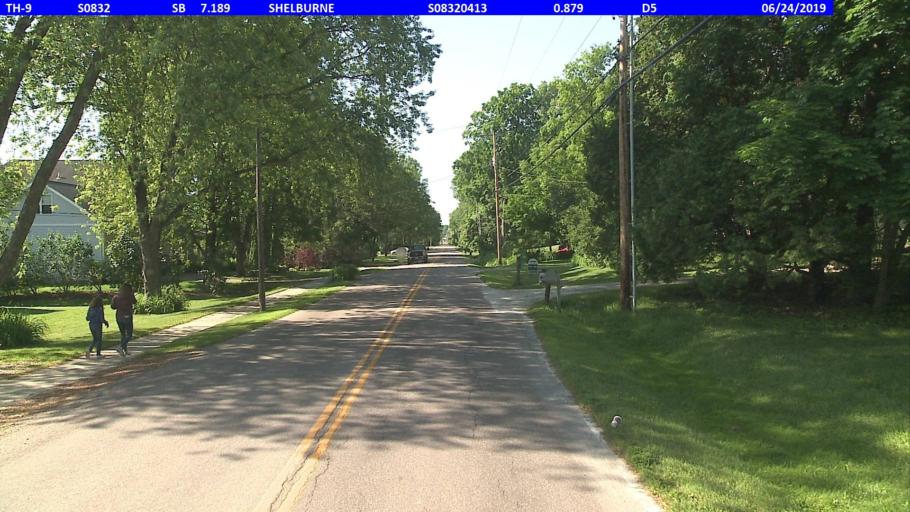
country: US
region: Vermont
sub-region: Chittenden County
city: Burlington
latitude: 44.3677
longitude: -73.2240
